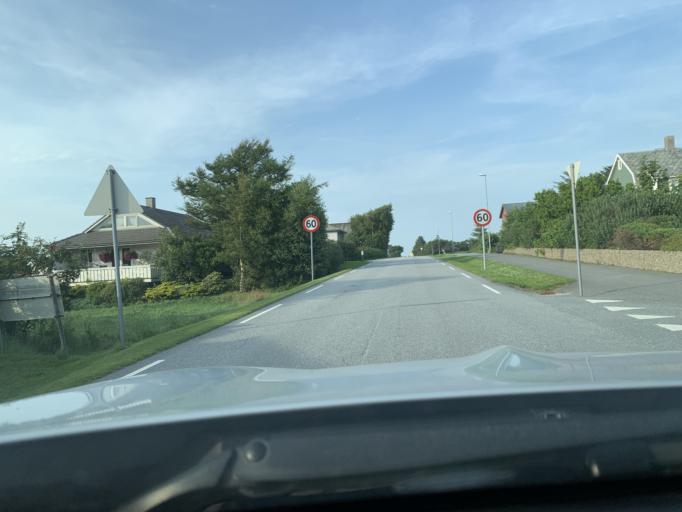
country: NO
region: Rogaland
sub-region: Time
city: Bryne
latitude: 58.7203
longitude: 5.5725
